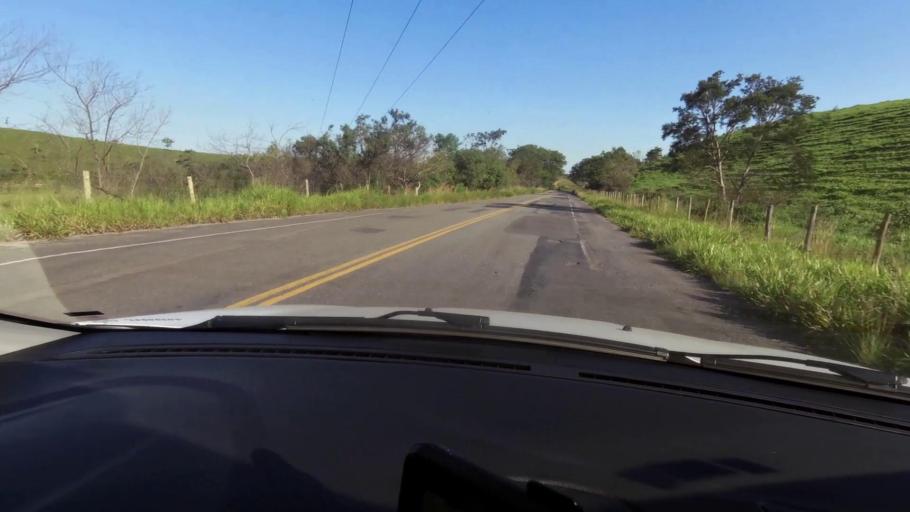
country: BR
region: Espirito Santo
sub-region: Piuma
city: Piuma
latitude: -20.7395
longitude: -40.6474
